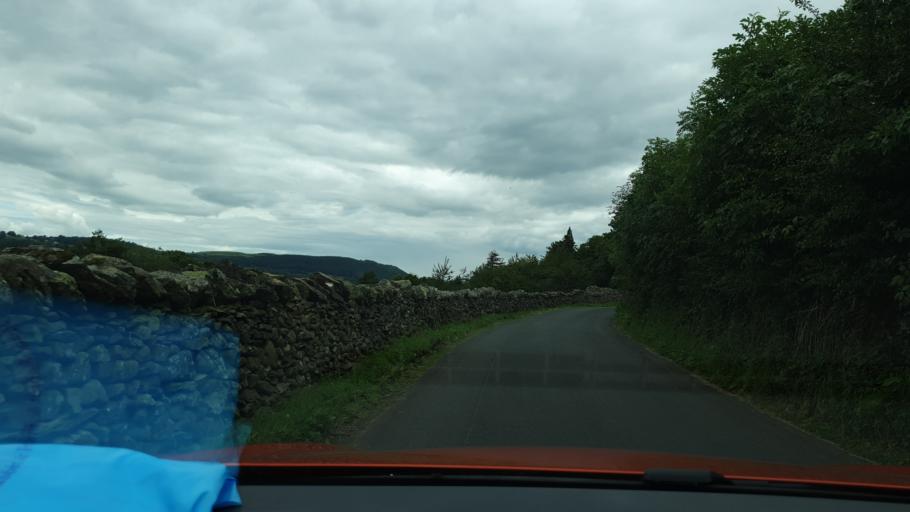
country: GB
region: England
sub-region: Cumbria
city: Penrith
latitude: 54.5740
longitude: -2.8596
